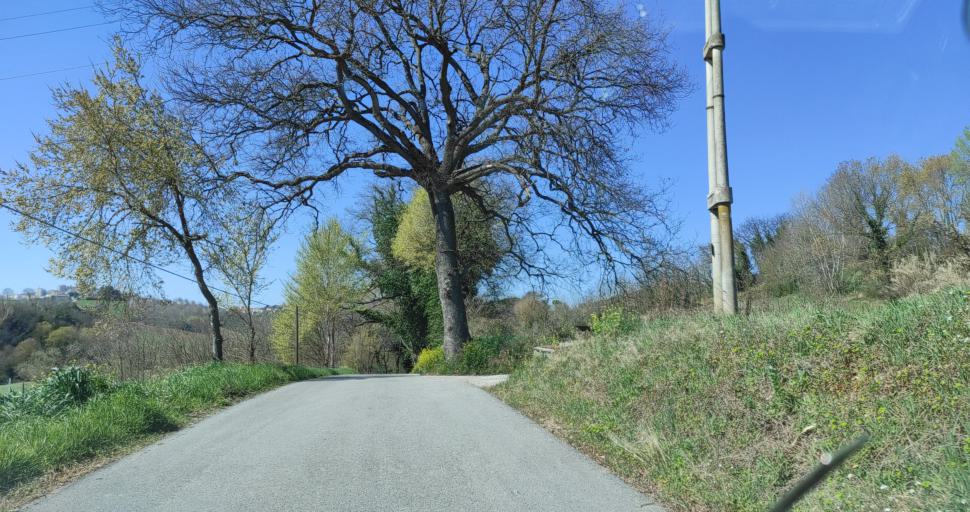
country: IT
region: The Marches
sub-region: Provincia di Macerata
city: Piediripa
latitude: 43.3123
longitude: 13.4887
